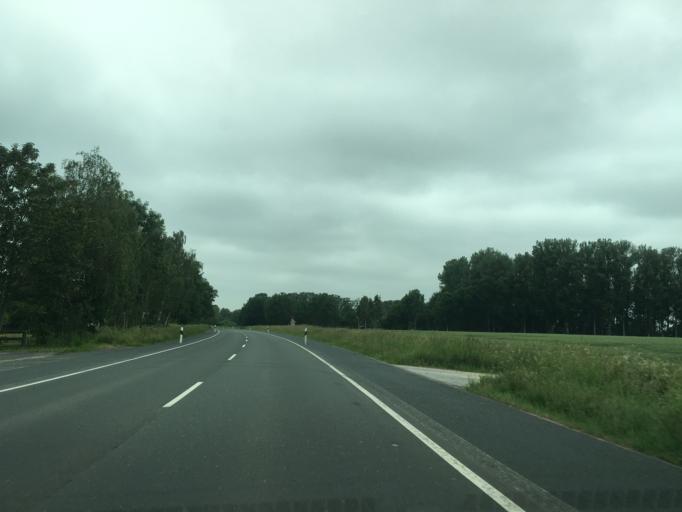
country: DE
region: North Rhine-Westphalia
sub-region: Regierungsbezirk Munster
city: Altenberge
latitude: 52.0470
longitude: 7.4381
